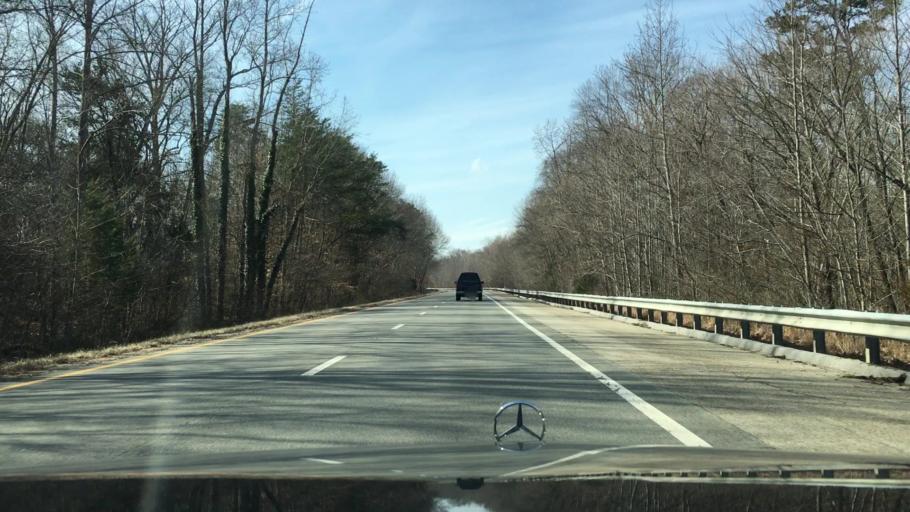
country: US
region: Virginia
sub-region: Prince Edward County
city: Hampden Sydney
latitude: 37.3140
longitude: -78.4867
